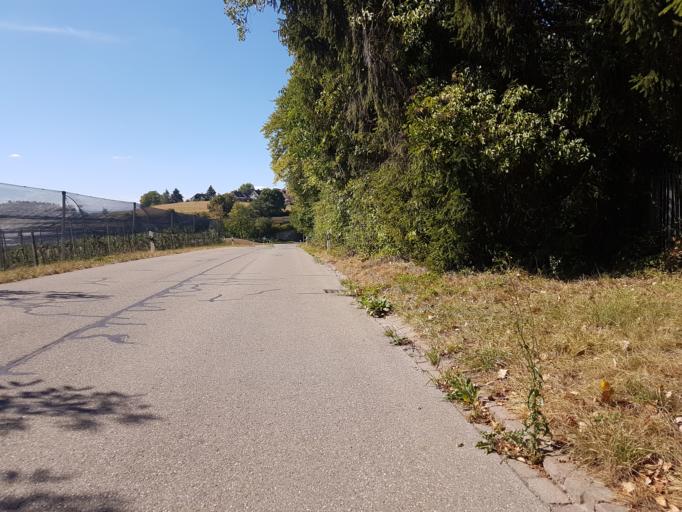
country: CH
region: Zurich
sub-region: Bezirk Pfaeffikon
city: Tagelswangen
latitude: 47.4239
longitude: 8.6775
